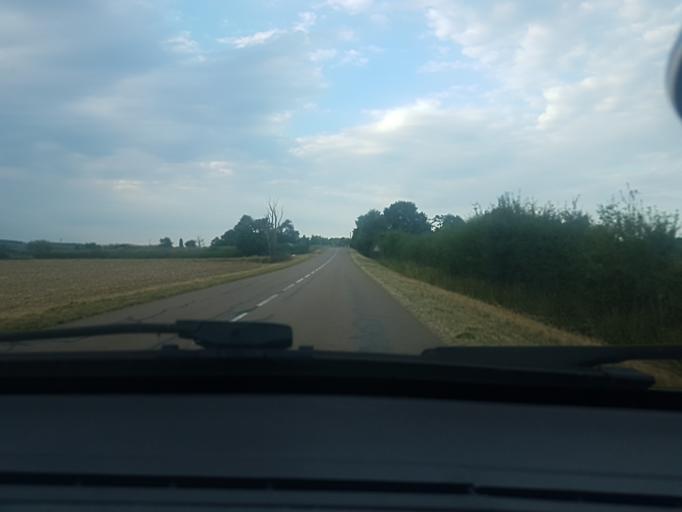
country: FR
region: Bourgogne
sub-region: Departement de Saone-et-Loire
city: Givry
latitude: 46.7578
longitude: 4.7427
